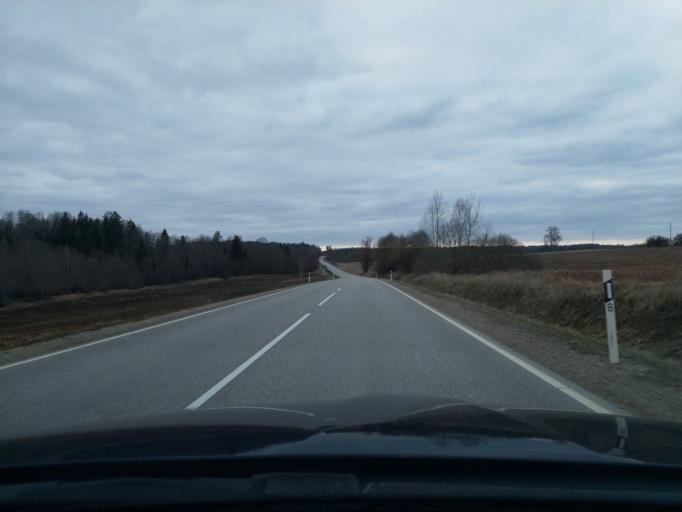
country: LV
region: Kuldigas Rajons
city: Kuldiga
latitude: 56.9649
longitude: 22.0642
